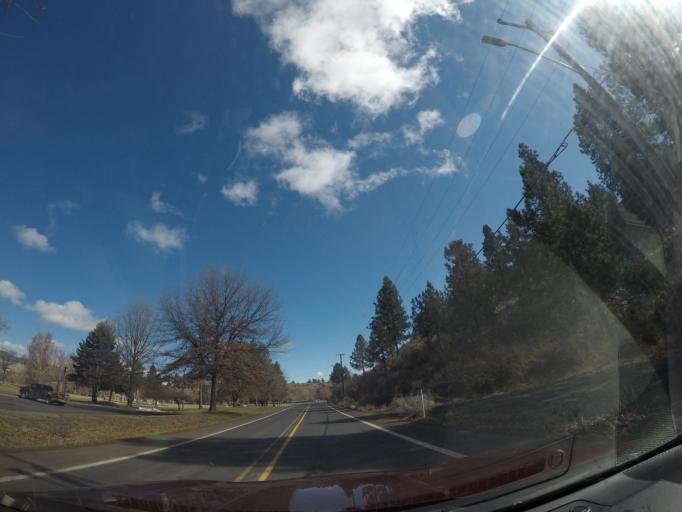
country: US
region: Oregon
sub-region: Klamath County
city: Klamath Falls
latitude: 42.2335
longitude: -121.8130
